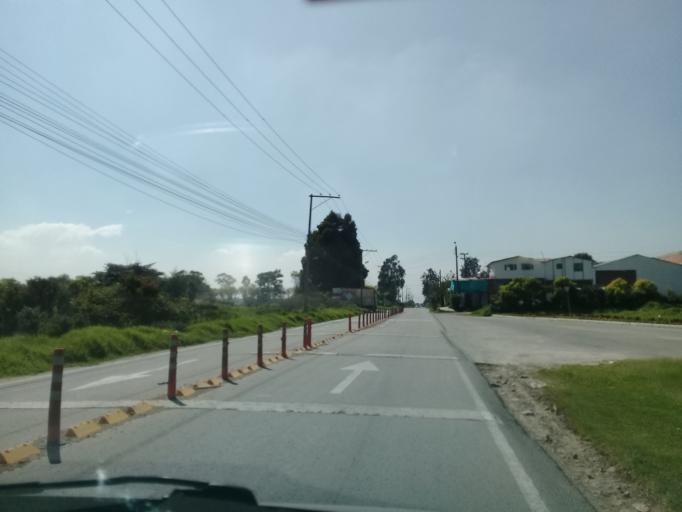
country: CO
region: Cundinamarca
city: Funza
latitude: 4.7448
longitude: -74.1629
